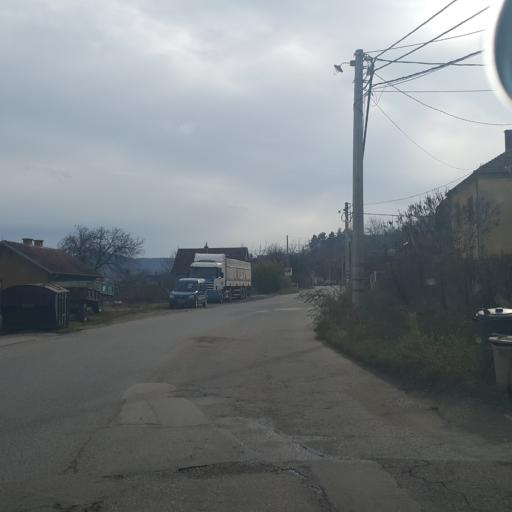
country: RS
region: Central Serbia
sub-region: Zajecarski Okrug
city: Knjazevac
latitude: 43.5743
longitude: 22.2476
